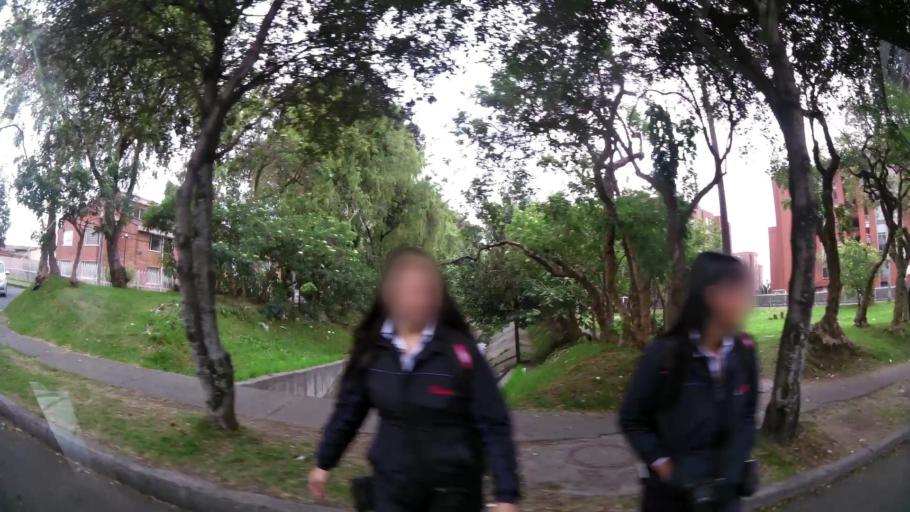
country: CO
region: Bogota D.C.
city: Bogota
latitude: 4.6723
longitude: -74.1214
